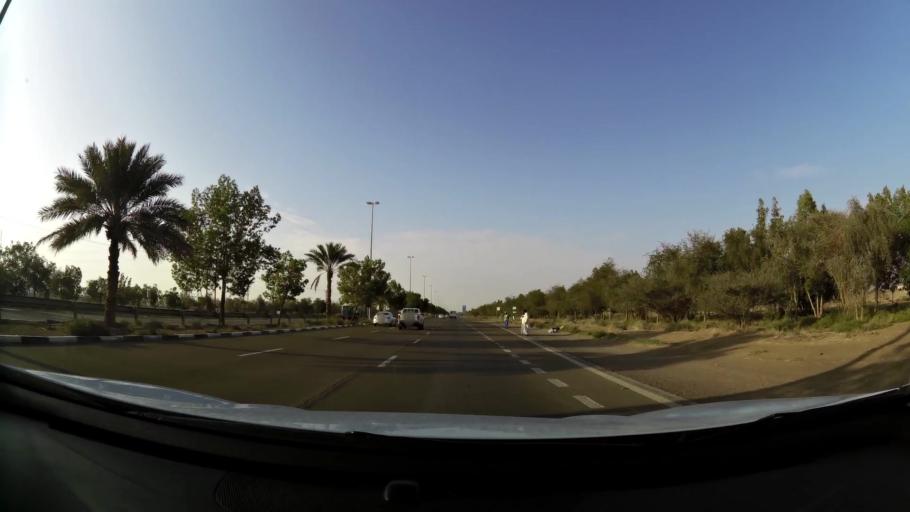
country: AE
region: Abu Dhabi
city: Al Ain
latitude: 24.1131
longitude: 55.8250
